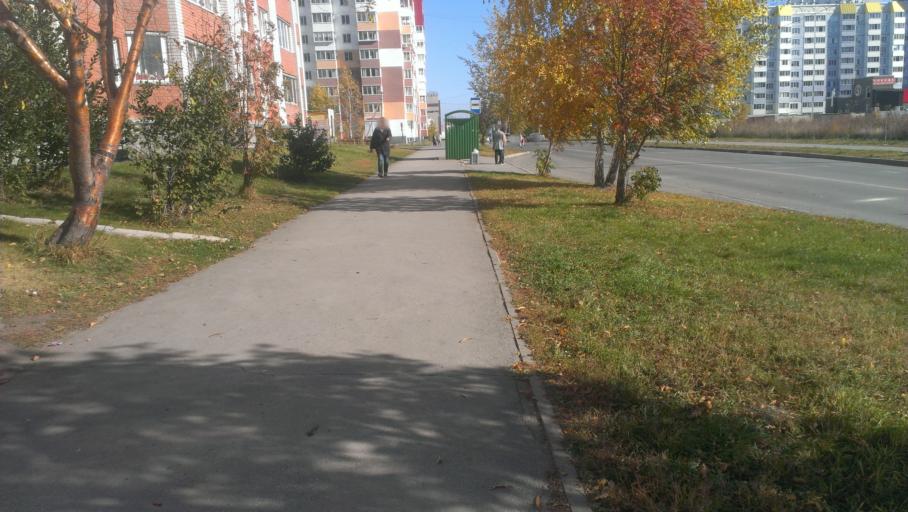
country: RU
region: Altai Krai
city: Novosilikatnyy
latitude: 53.3301
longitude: 83.6827
